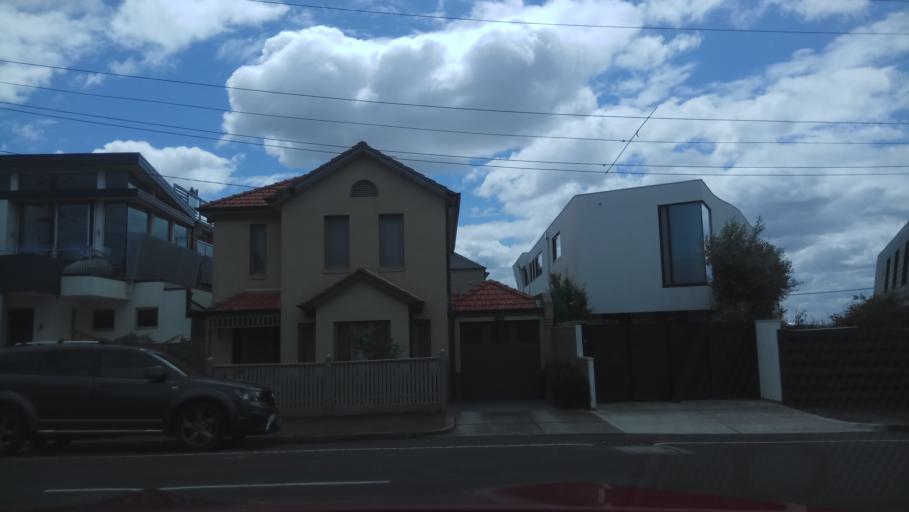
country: AU
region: Victoria
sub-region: Hobsons Bay
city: Williamstown
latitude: -37.8513
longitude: 144.8967
